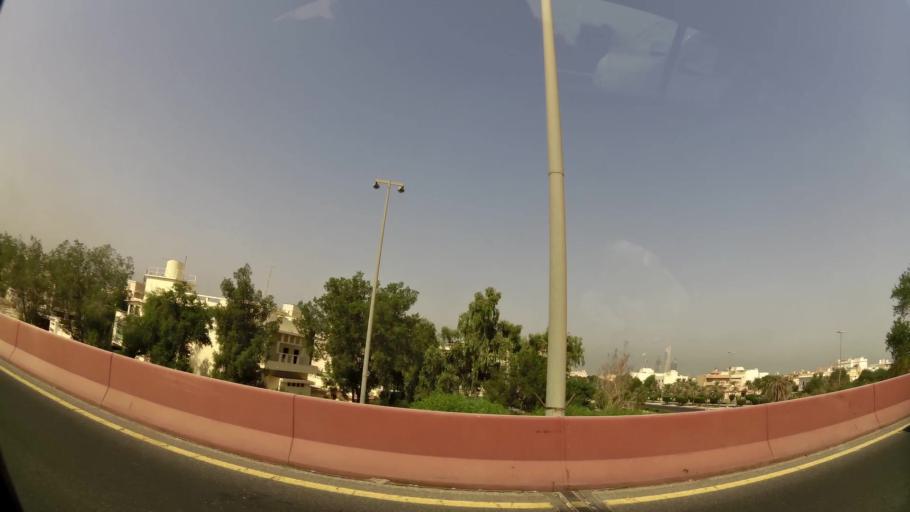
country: KW
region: Al Asimah
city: Ash Shamiyah
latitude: 29.3347
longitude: 47.9865
